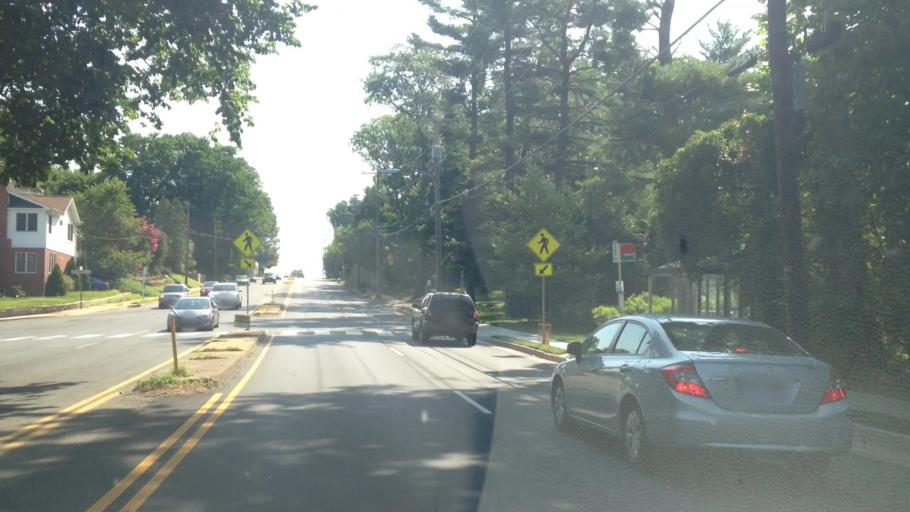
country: US
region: Virginia
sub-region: Fairfax County
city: Seven Corners
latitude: 38.8935
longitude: -77.1479
